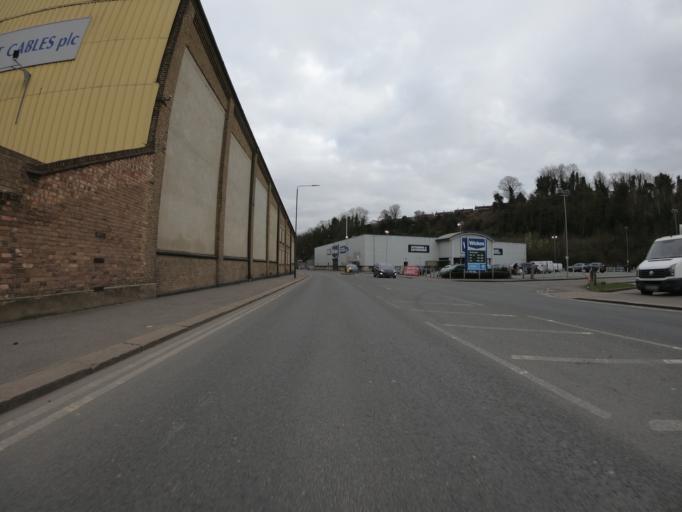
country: GB
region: England
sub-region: Greater London
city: Erith
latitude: 51.4821
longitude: 0.1680
